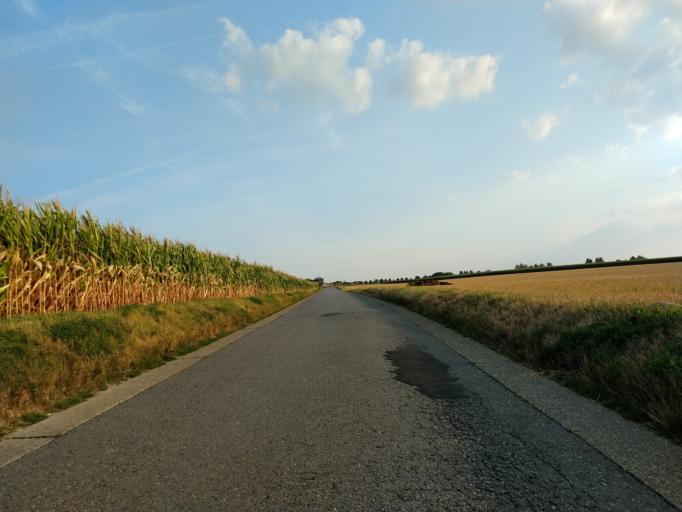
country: BE
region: Flanders
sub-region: Provincie Vlaams-Brabant
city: Hoegaarden
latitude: 50.7939
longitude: 4.8702
